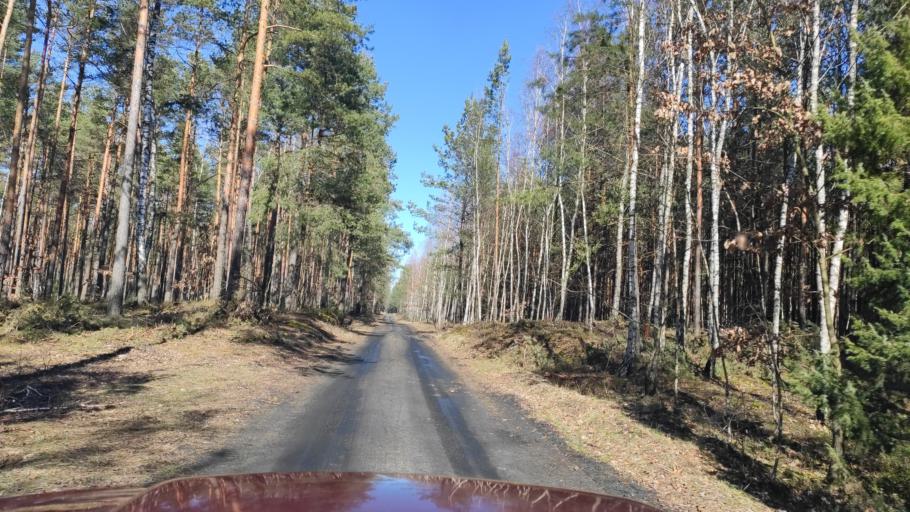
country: PL
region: Masovian Voivodeship
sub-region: Powiat zwolenski
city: Zwolen
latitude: 51.4128
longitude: 21.5558
